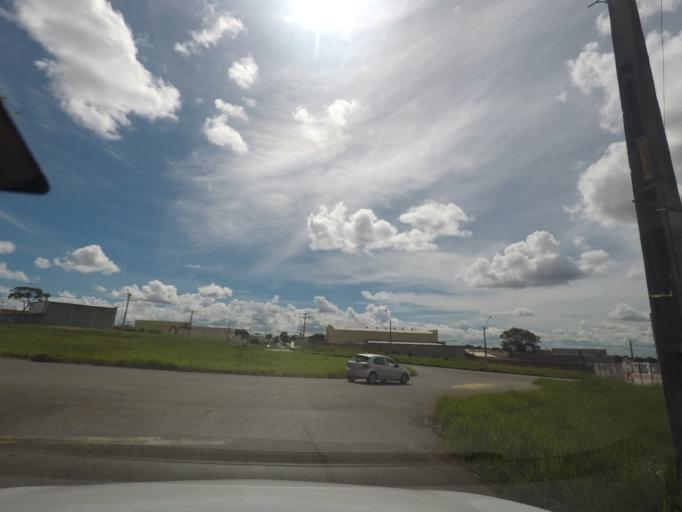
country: BR
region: Goias
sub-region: Goiania
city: Goiania
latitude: -16.7445
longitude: -49.3344
